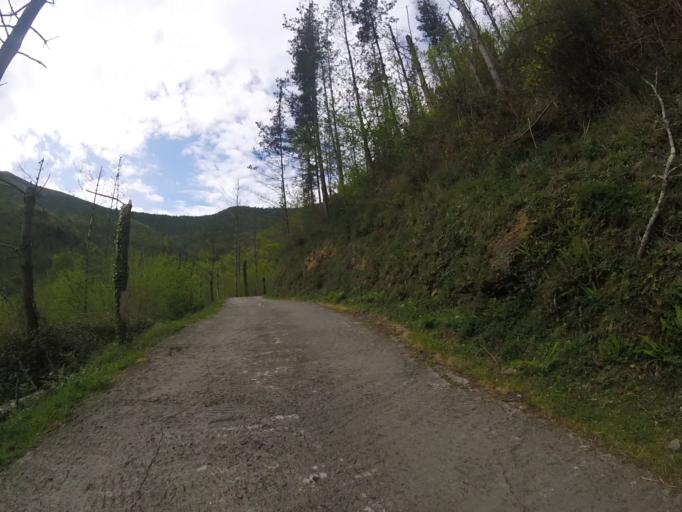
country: ES
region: Basque Country
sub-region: Provincia de Guipuzcoa
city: Errezil
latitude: 43.2013
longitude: -2.1859
